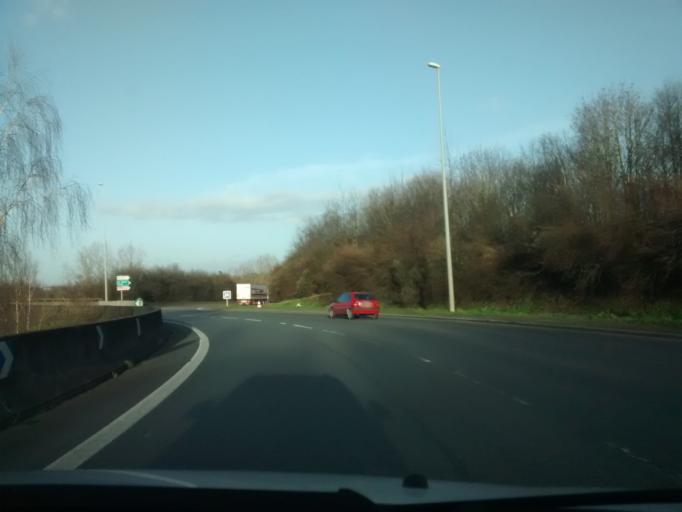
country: FR
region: Brittany
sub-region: Departement d'Ille-et-Vilaine
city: Chantepie
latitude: 48.1014
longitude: -1.6084
